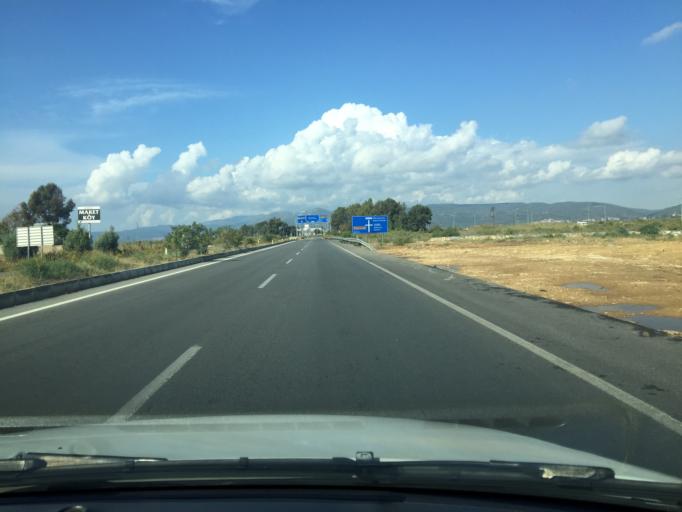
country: TR
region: Izmir
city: Selcuk
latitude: 37.9492
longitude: 27.3028
